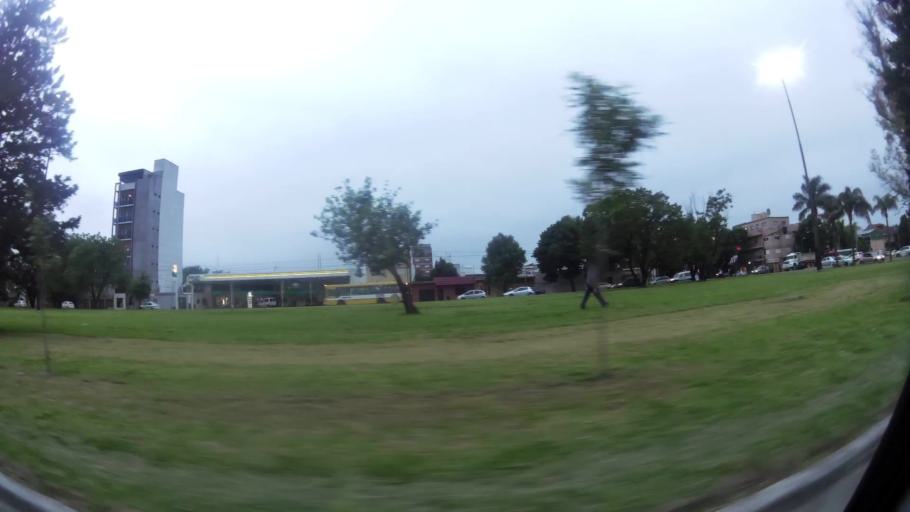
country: AR
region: Buenos Aires
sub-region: Partido de La Plata
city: La Plata
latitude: -34.9111
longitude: -57.9813
